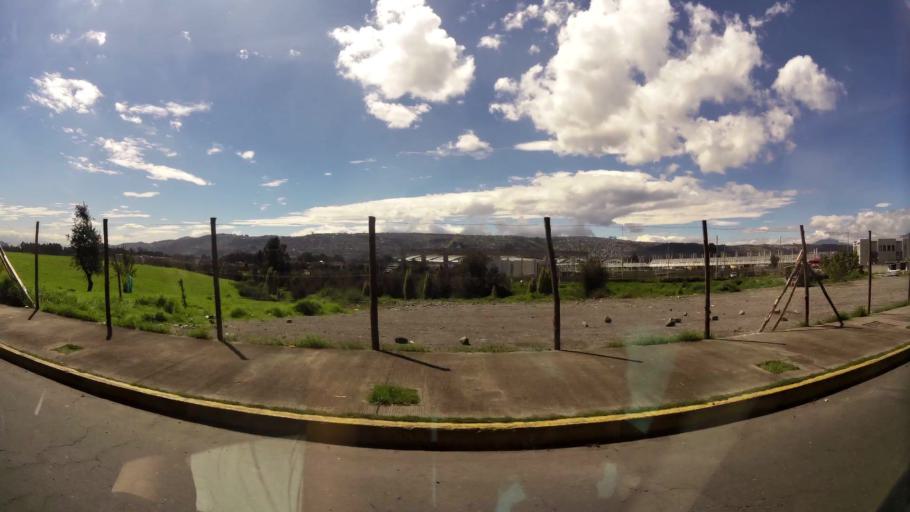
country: EC
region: Pichincha
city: Quito
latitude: -0.2953
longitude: -78.5587
